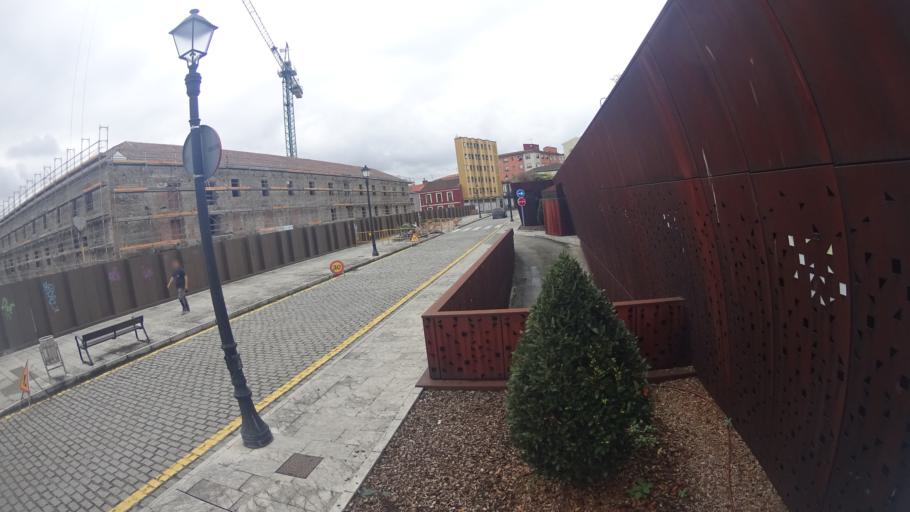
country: ES
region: Asturias
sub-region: Province of Asturias
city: Gijon
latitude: 43.5472
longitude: -5.6624
